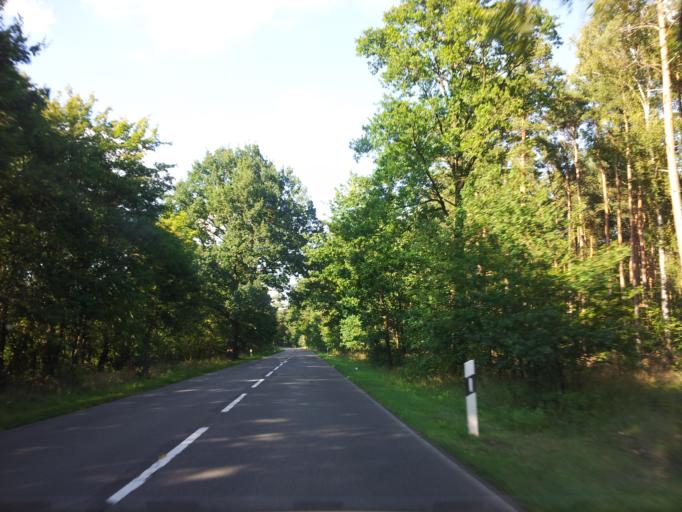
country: DE
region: Brandenburg
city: Niedergorsdorf
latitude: 51.9842
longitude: 13.0051
